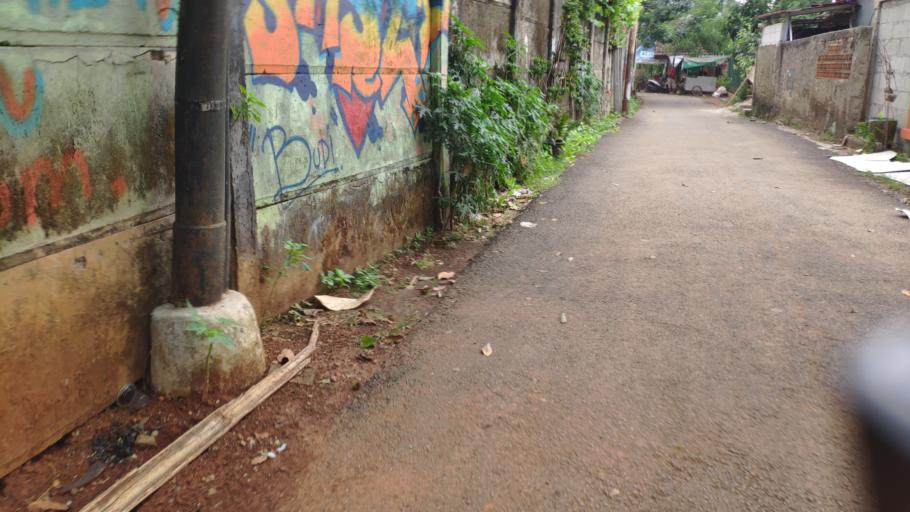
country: ID
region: West Java
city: Depok
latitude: -6.3207
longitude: 106.8232
